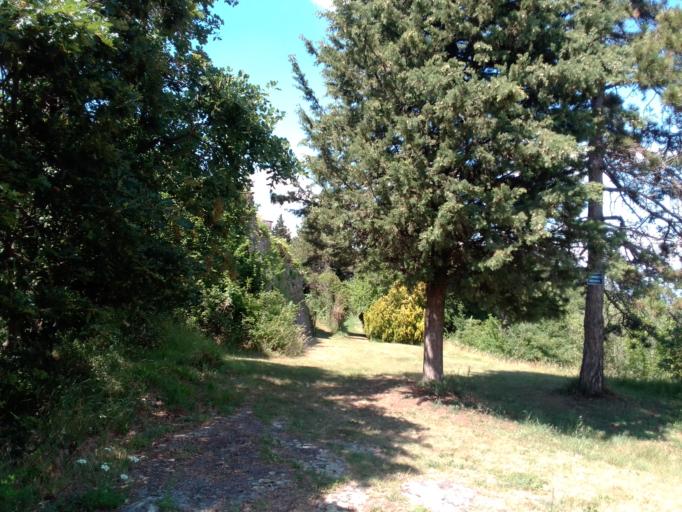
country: IT
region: Emilia-Romagna
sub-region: Provincia di Piacenza
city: Pianello Val Tidone
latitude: 44.9130
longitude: 9.3939
